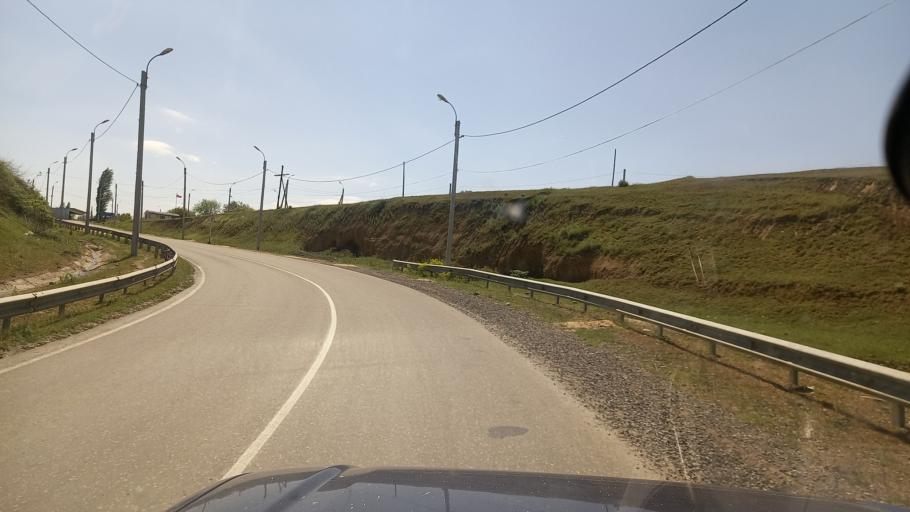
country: RU
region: Dagestan
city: Novaya Maka
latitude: 41.7378
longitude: 48.4430
